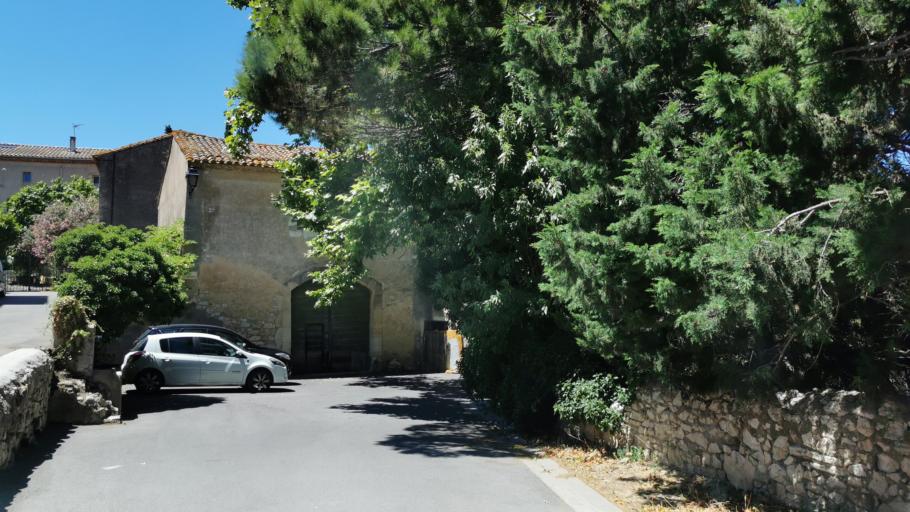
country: FR
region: Languedoc-Roussillon
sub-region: Departement de l'Aude
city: Peyriac-de-Mer
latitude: 43.1308
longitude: 2.9753
